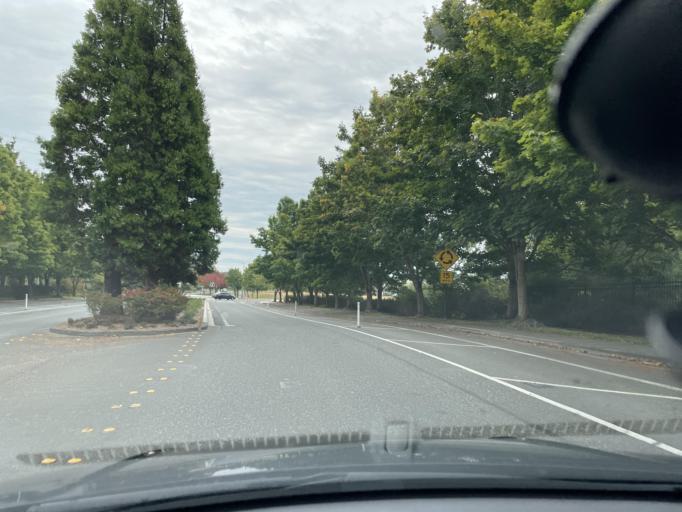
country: US
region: Washington
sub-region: Whatcom County
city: Bellingham
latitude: 48.8068
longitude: -122.4977
